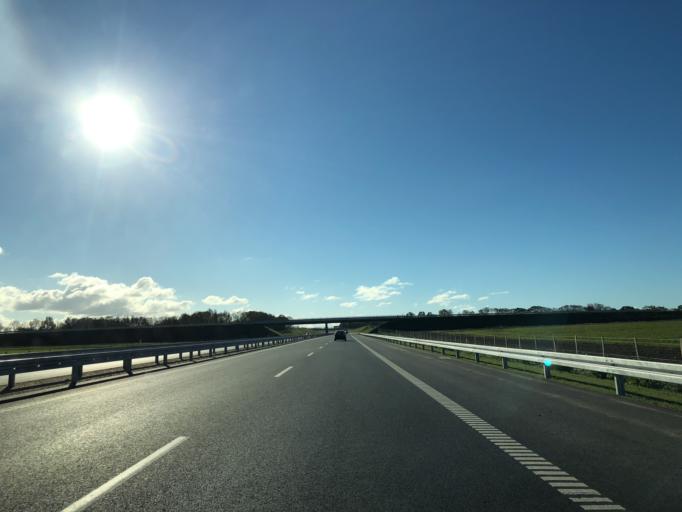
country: DK
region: Central Jutland
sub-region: Herning Kommune
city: Avlum
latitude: 56.3196
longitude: 8.7320
